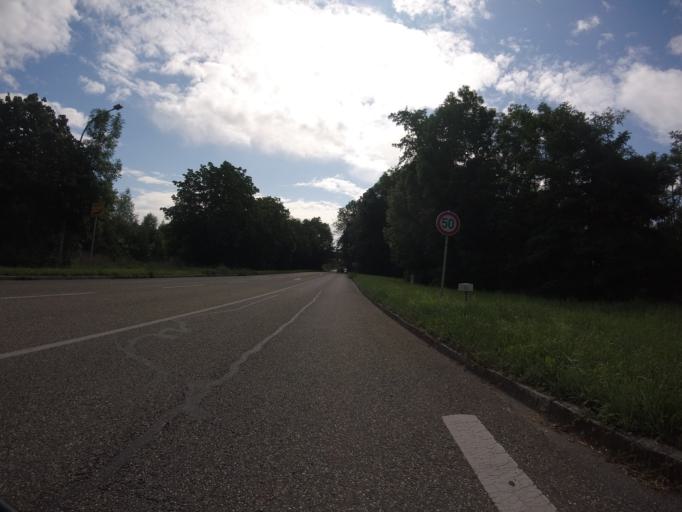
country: DE
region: Baden-Wuerttemberg
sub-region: Regierungsbezirk Stuttgart
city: Leutenbach
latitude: 48.8836
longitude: 9.3938
